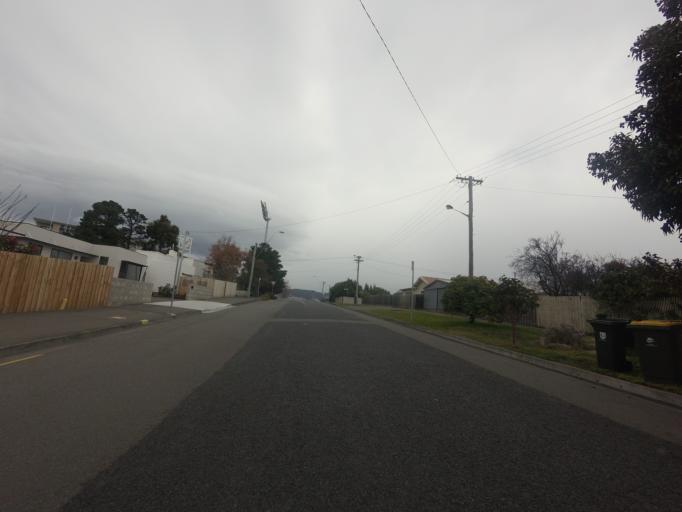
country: AU
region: Tasmania
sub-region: Clarence
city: Bellerive
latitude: -42.8756
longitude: 147.3731
